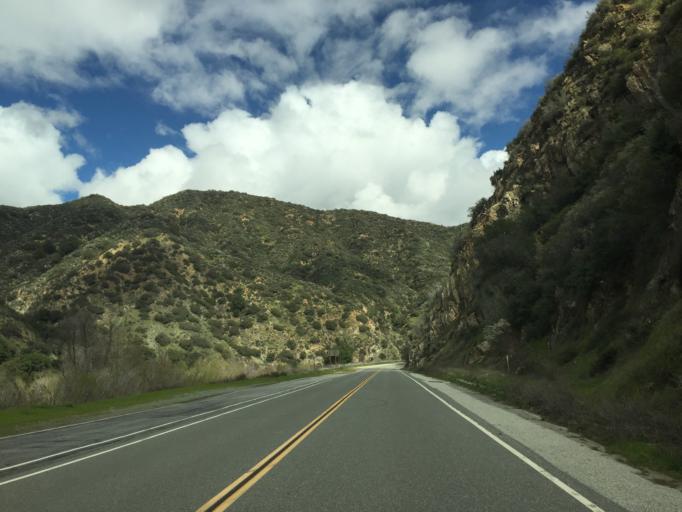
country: US
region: California
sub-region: Los Angeles County
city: Glendora
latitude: 34.2391
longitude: -117.8574
